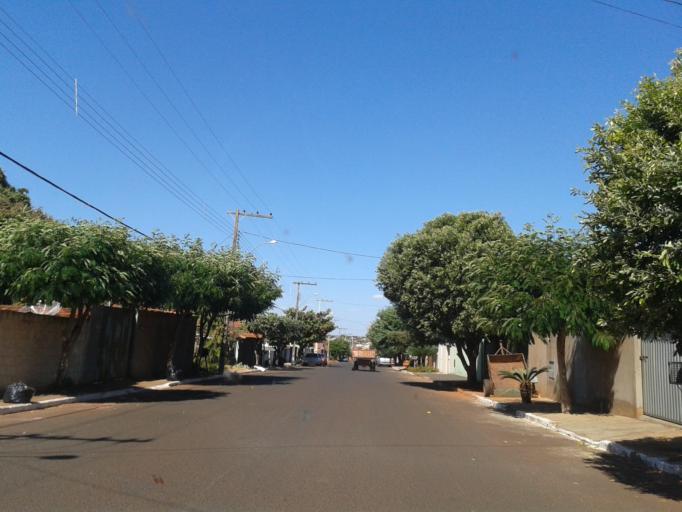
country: BR
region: Minas Gerais
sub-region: Santa Vitoria
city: Santa Vitoria
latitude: -18.8352
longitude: -50.1360
